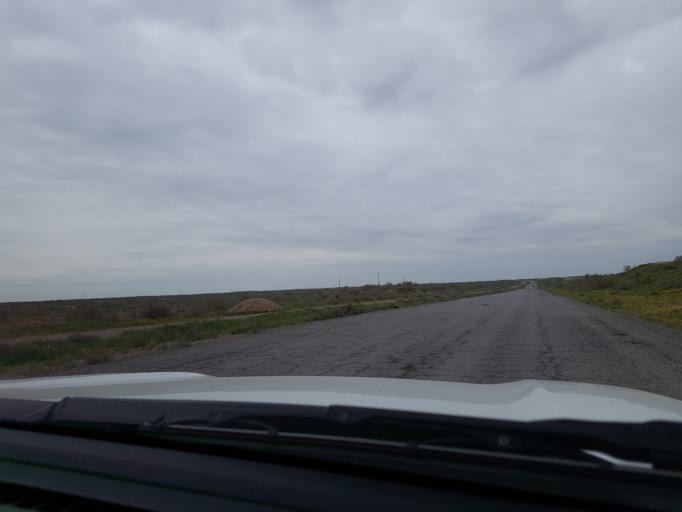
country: TM
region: Mary
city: Bayramaly
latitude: 37.9066
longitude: 62.6192
